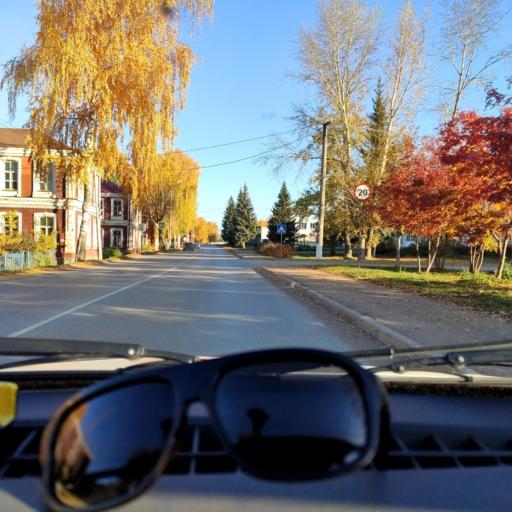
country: RU
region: Bashkortostan
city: Blagoveshchensk
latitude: 55.0297
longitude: 55.9717
